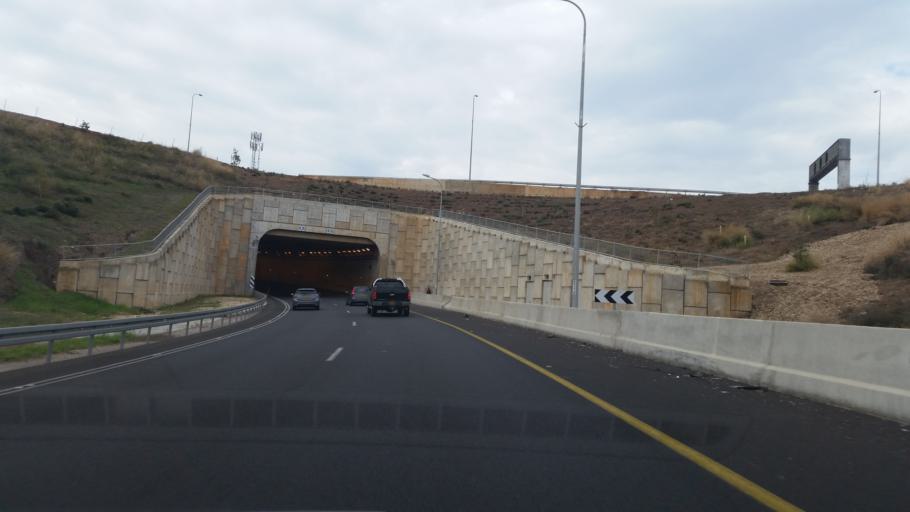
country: IL
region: Tel Aviv
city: Kefar Shemaryahu
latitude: 32.1946
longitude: 34.8320
